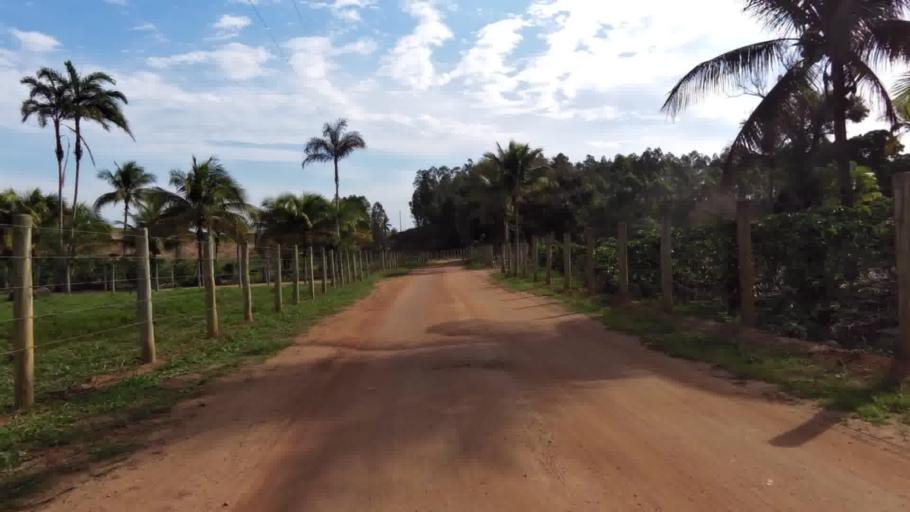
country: BR
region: Espirito Santo
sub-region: Piuma
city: Piuma
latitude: -20.8198
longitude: -40.7413
